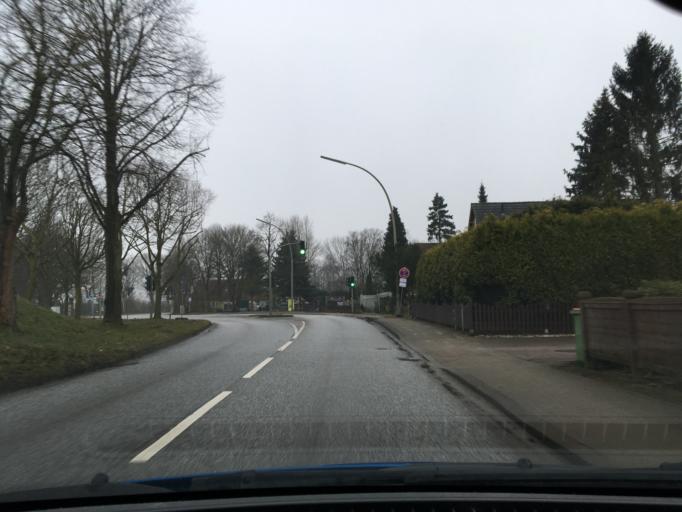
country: DE
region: Hamburg
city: Altona
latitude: 53.5032
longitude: 9.8766
